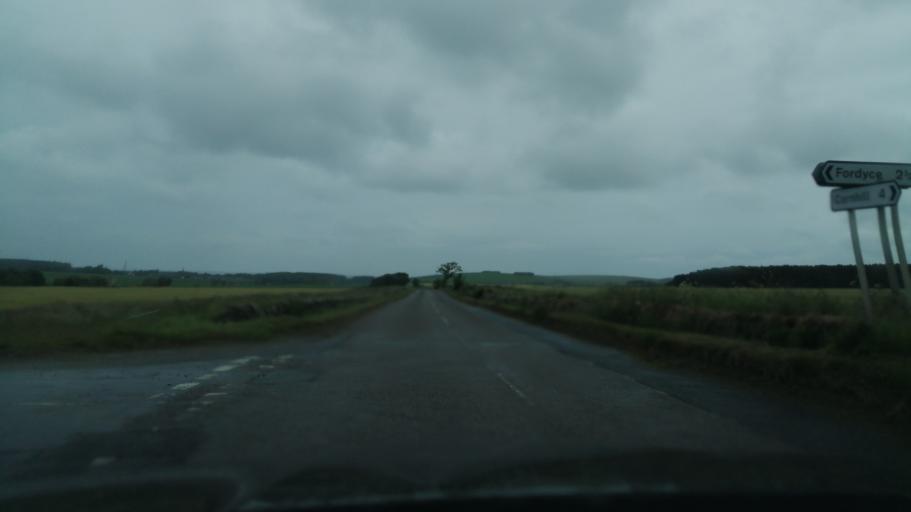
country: GB
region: Scotland
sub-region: Aberdeenshire
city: Portsoy
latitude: 57.6572
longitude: -2.7003
